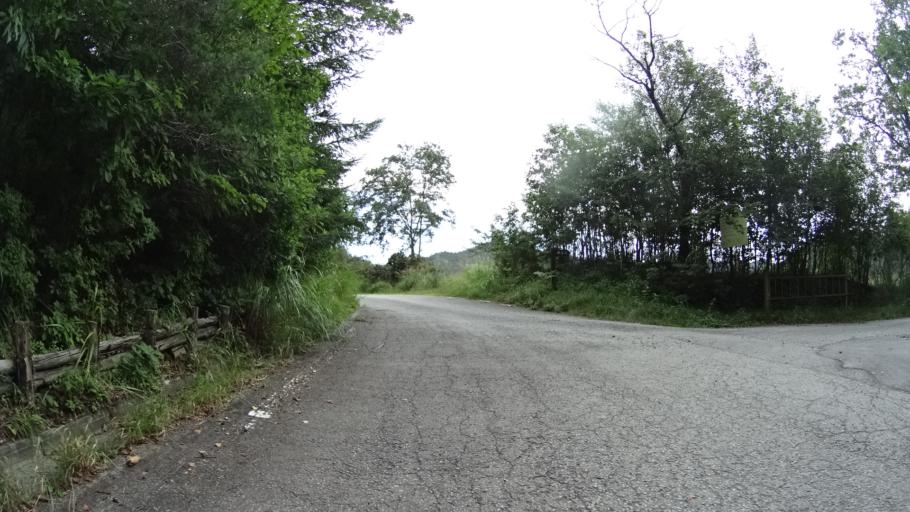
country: JP
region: Yamanashi
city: Kofu-shi
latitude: 35.8183
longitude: 138.5532
